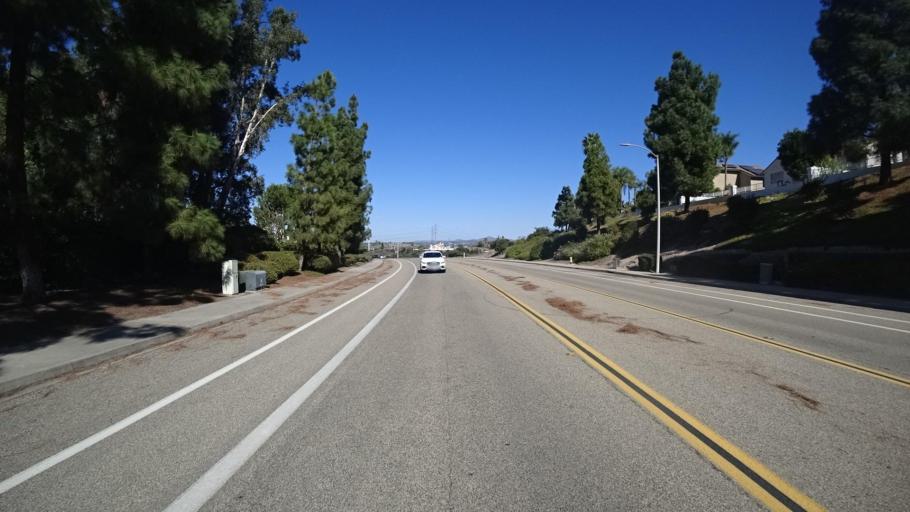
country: US
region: California
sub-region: San Diego County
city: Bonita
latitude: 32.6552
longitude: -116.9906
